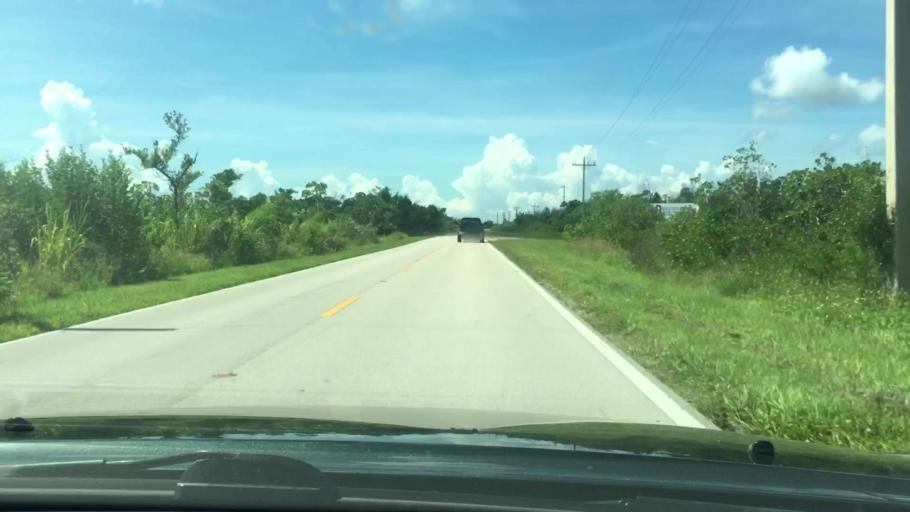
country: US
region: Florida
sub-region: Collier County
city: Marco
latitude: 25.9402
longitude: -81.6461
